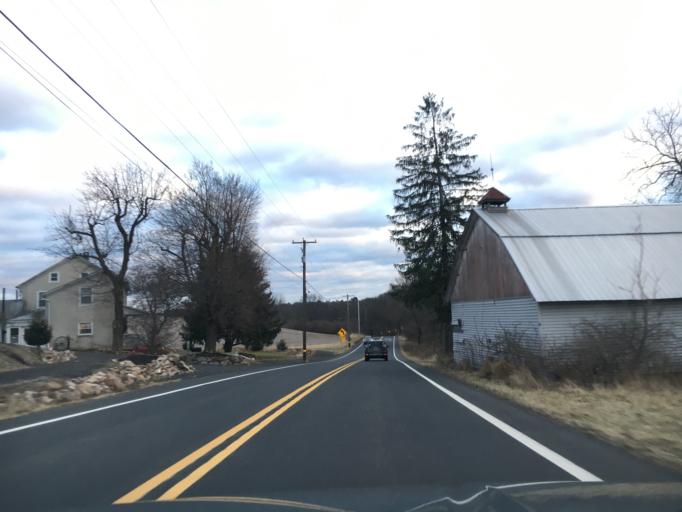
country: US
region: Pennsylvania
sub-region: Lehigh County
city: Schnecksville
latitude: 40.6802
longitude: -75.6523
